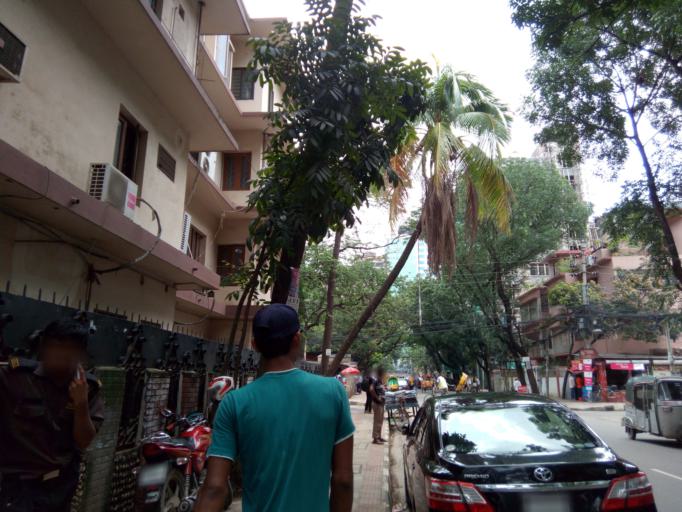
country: BD
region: Dhaka
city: Paltan
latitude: 23.7911
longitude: 90.4041
